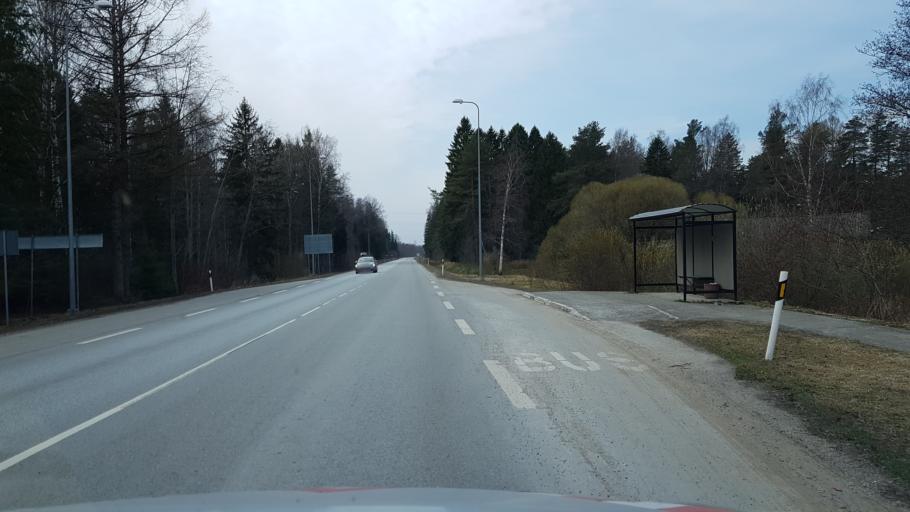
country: EE
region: Ida-Virumaa
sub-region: Aseri vald
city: Aseri
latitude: 59.3508
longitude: 26.8206
